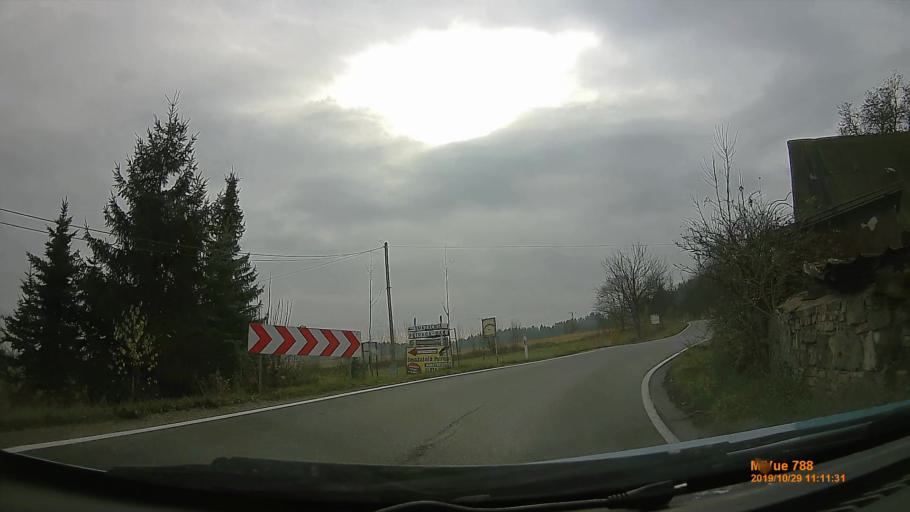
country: PL
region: Lower Silesian Voivodeship
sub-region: Powiat klodzki
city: Polanica-Zdroj
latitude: 50.4345
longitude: 16.5041
